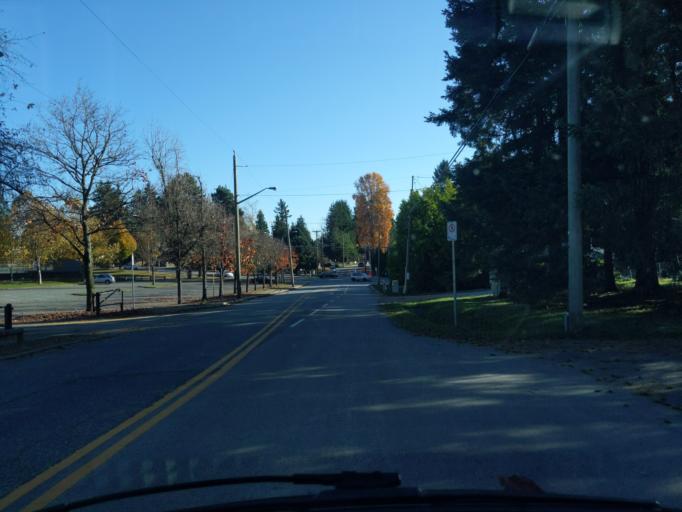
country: CA
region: British Columbia
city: New Westminster
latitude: 49.1925
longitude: -122.8643
